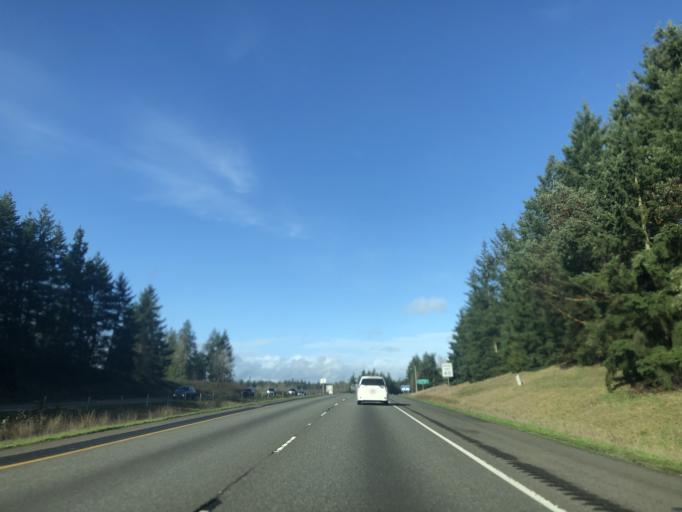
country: US
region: Washington
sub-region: Pierce County
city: Gig Harbor
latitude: 47.3347
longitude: -122.6028
